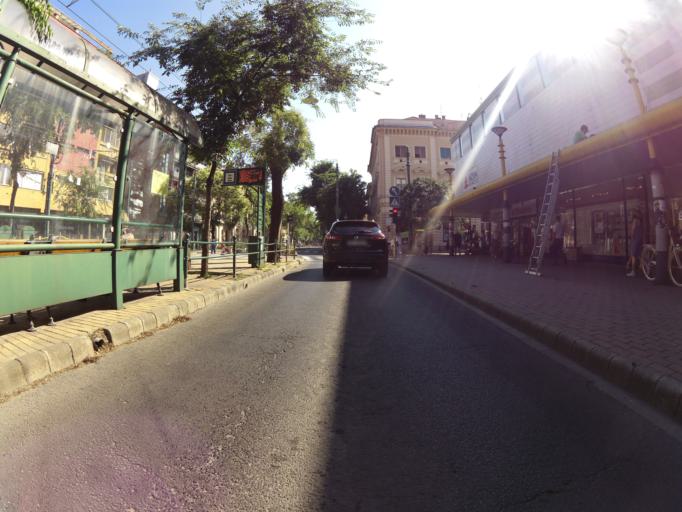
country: HU
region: Csongrad
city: Szeged
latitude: 46.2546
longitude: 20.1464
